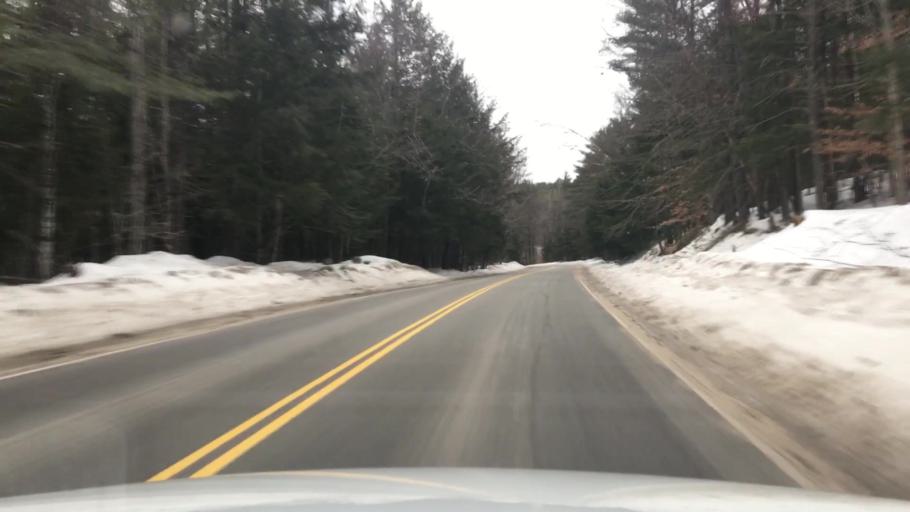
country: US
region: Maine
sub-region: Oxford County
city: Hiram
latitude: 43.8884
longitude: -70.7911
